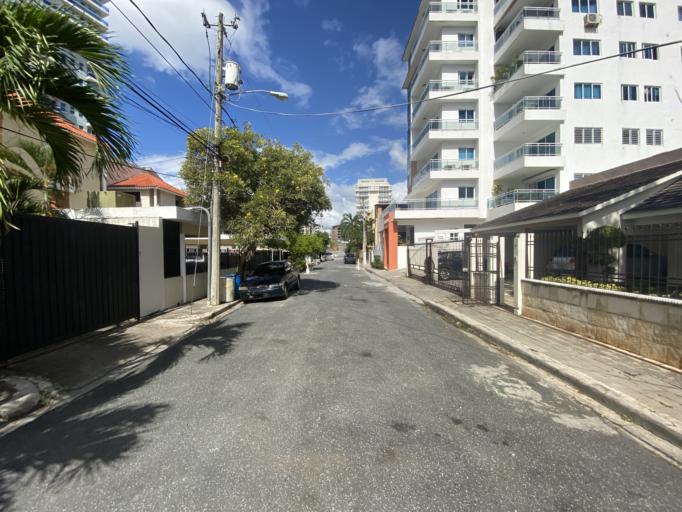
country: DO
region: Nacional
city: Ciudad Nueva
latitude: 18.4702
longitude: -69.9154
